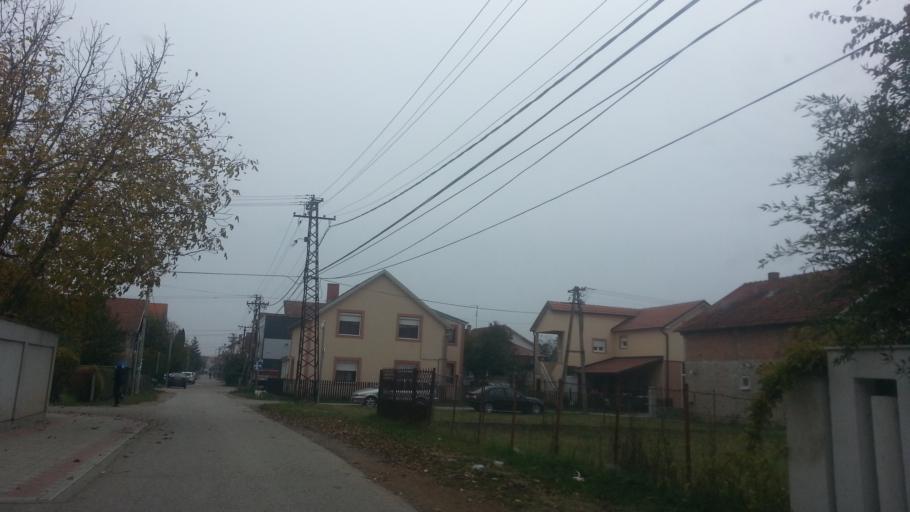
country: RS
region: Autonomna Pokrajina Vojvodina
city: Nova Pazova
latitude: 44.9551
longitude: 20.2161
